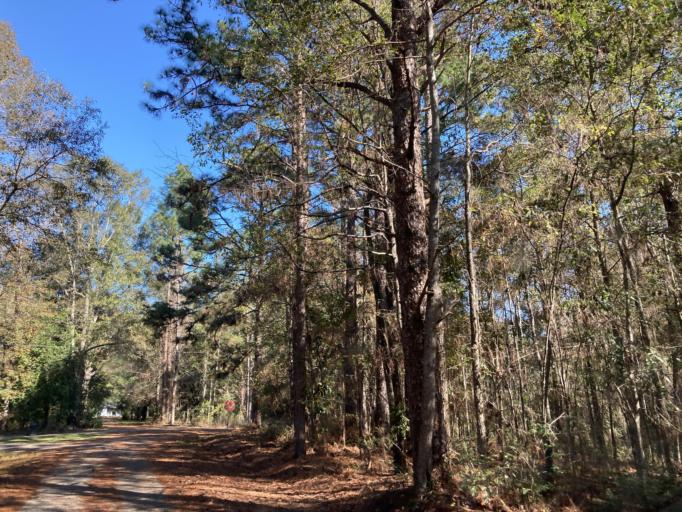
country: US
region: Mississippi
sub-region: Lamar County
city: Sumrall
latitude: 31.3351
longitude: -89.5142
